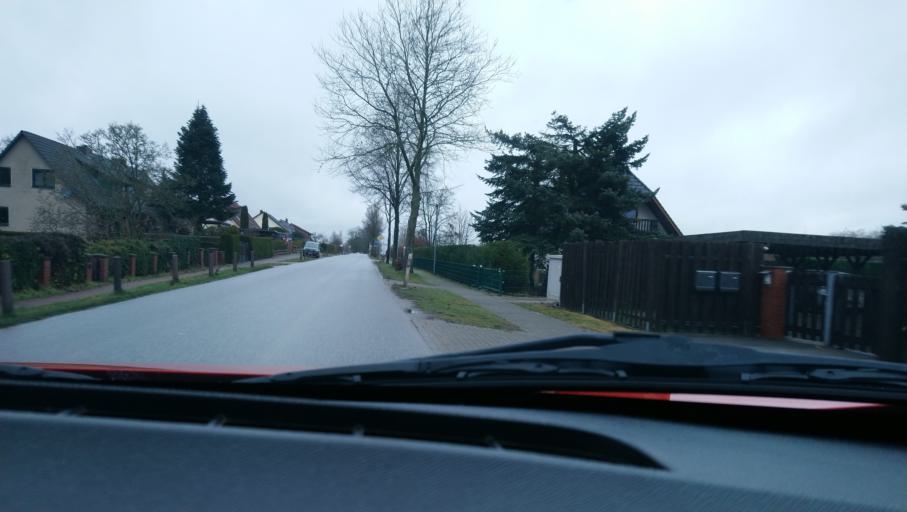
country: DE
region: Mecklenburg-Vorpommern
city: Seehof
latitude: 53.6946
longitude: 11.4316
